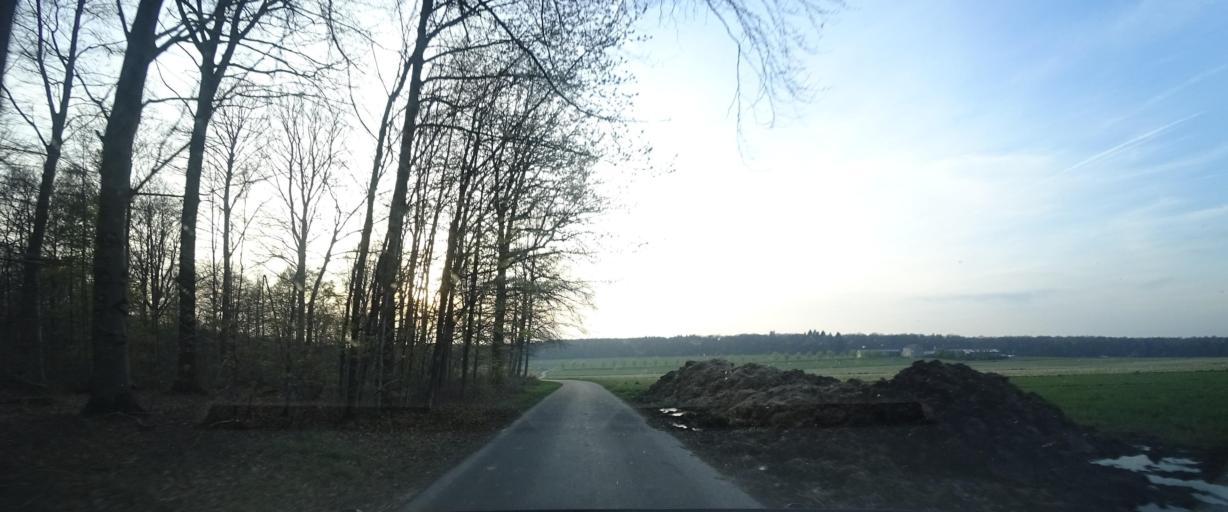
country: BE
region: Wallonia
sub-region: Province de Namur
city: Havelange
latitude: 50.3347
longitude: 5.2240
